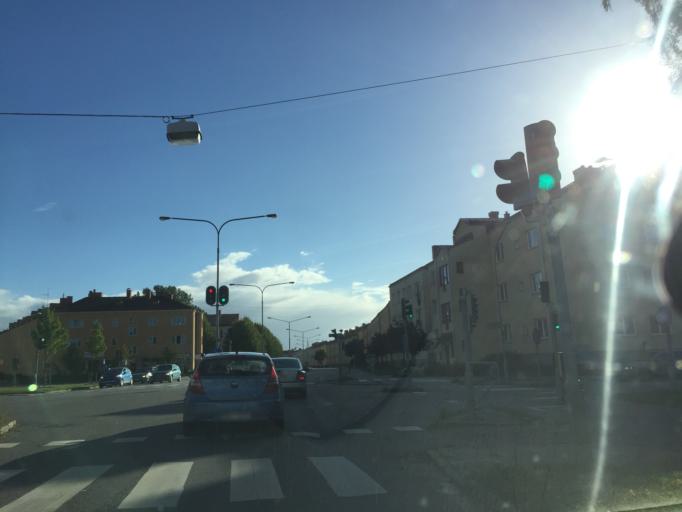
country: SE
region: OErebro
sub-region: Orebro Kommun
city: Orebro
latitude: 59.2850
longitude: 15.2032
